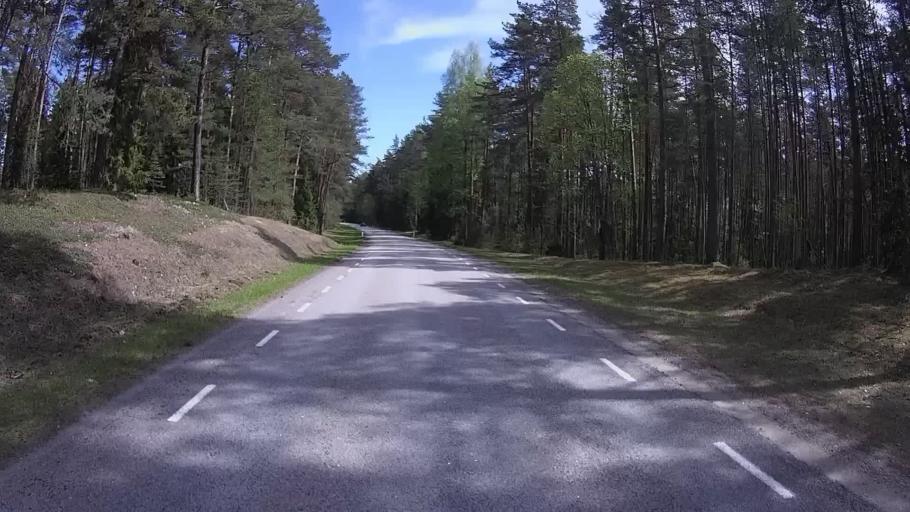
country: LV
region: Apes Novads
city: Ape
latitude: 57.6052
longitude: 26.4690
